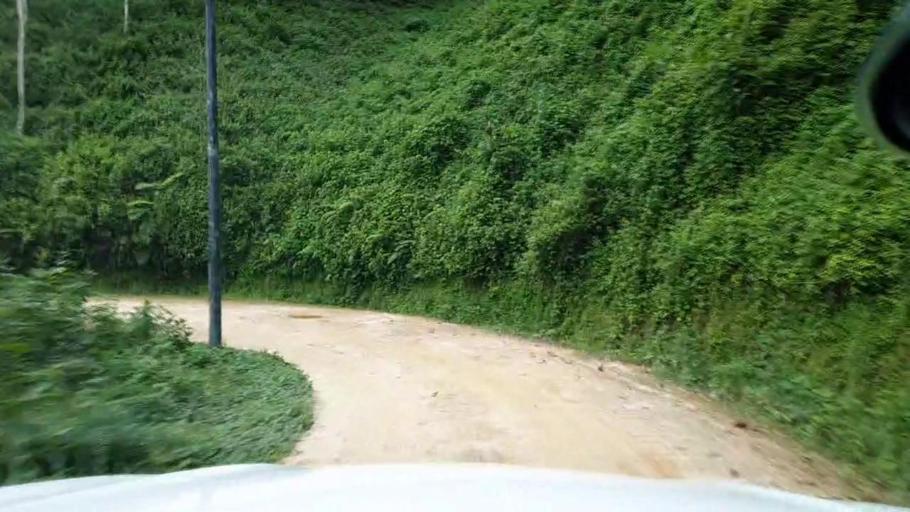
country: RW
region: Southern Province
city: Nzega
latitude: -2.5542
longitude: 29.2351
